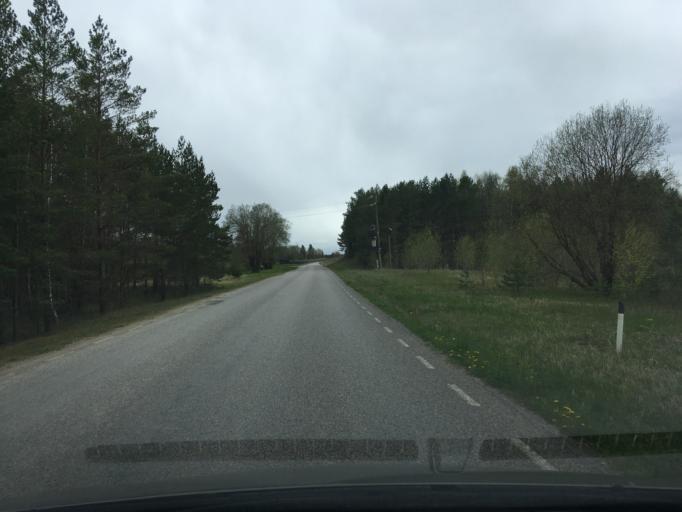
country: EE
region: Harju
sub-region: Rae vald
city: Vaida
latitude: 59.3266
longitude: 24.9995
